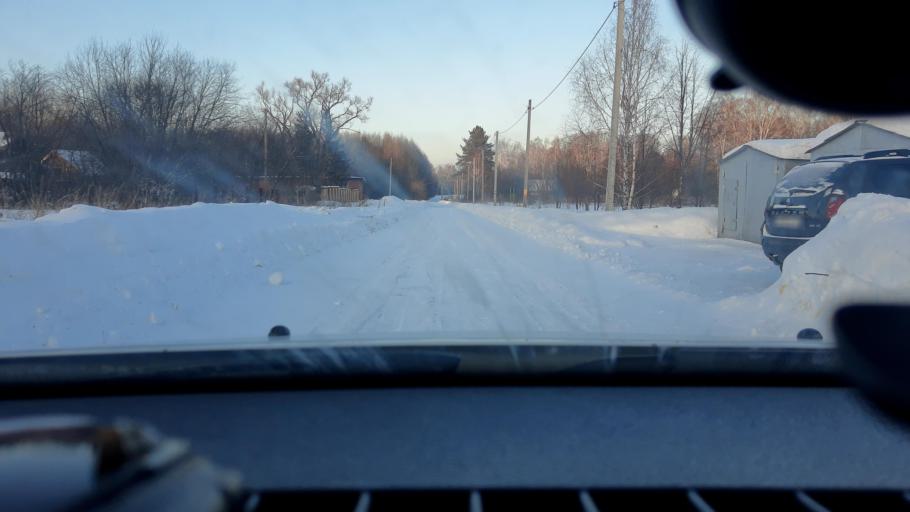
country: RU
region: Bashkortostan
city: Kudeyevskiy
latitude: 54.7979
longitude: 56.6750
